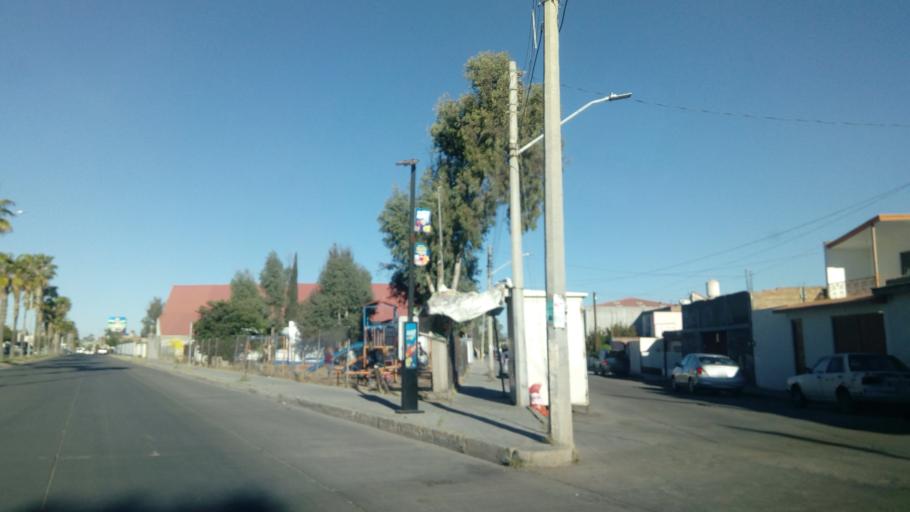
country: MX
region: Durango
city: Victoria de Durango
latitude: 24.0104
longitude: -104.6905
